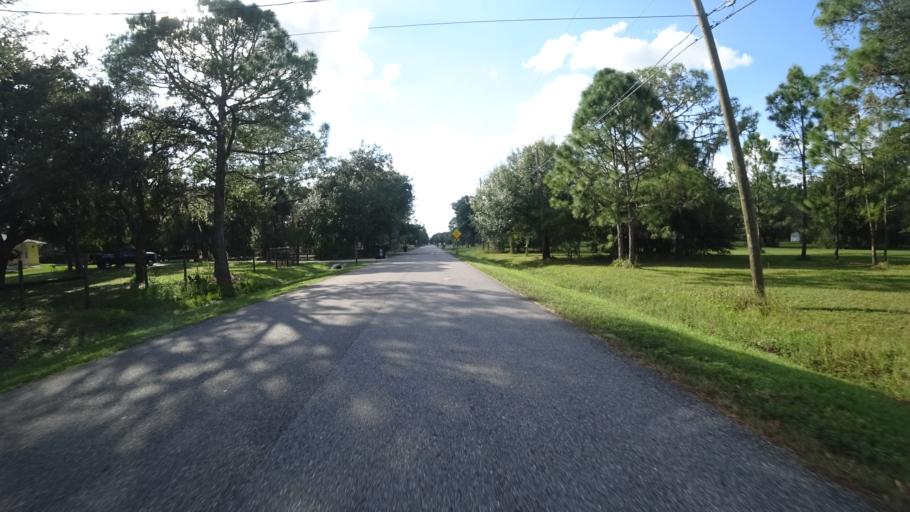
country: US
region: Florida
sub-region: Manatee County
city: Ellenton
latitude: 27.4874
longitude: -82.4807
